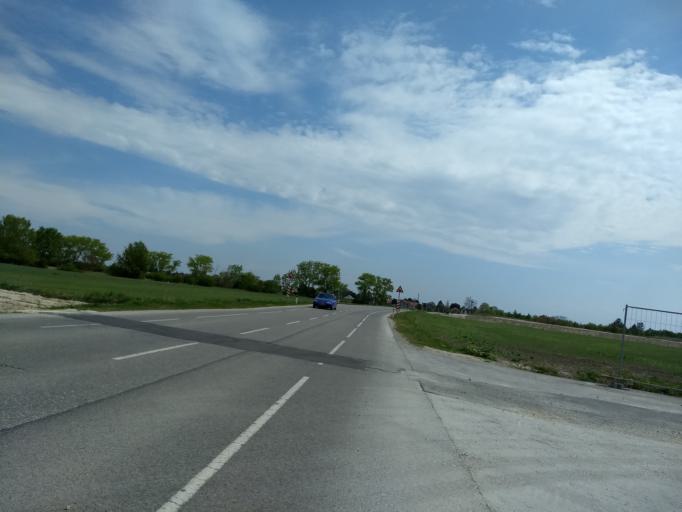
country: AT
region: Lower Austria
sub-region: Politischer Bezirk Ganserndorf
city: Gross-Enzersdorf
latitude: 48.2332
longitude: 16.5115
